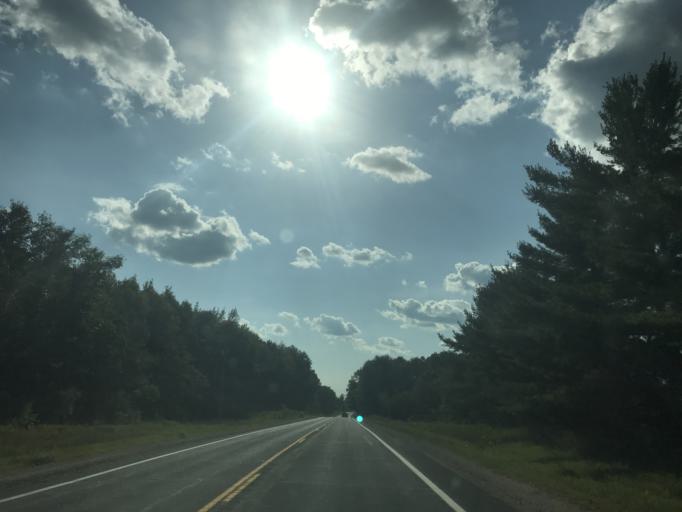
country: US
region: Michigan
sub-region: Newaygo County
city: White Cloud
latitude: 43.5683
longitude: -85.7977
